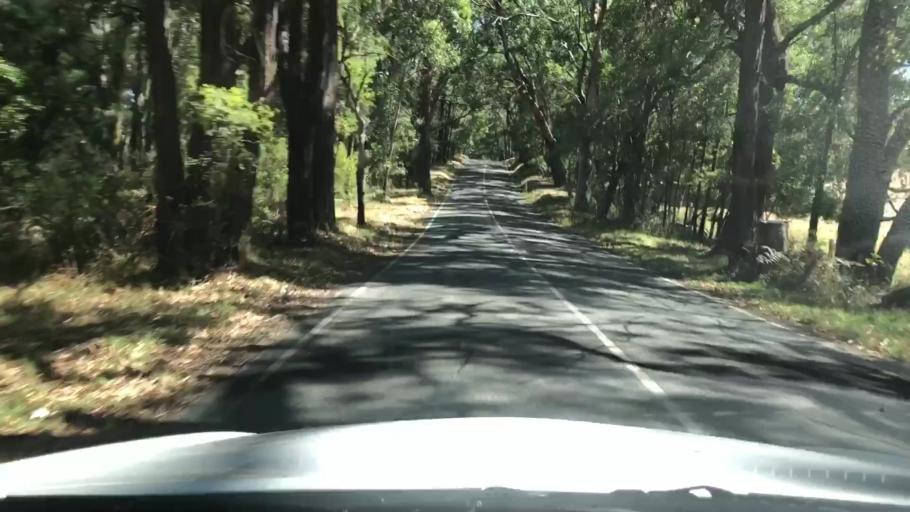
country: AU
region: Victoria
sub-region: Yarra Ranges
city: Macclesfield
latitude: -37.8574
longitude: 145.4811
